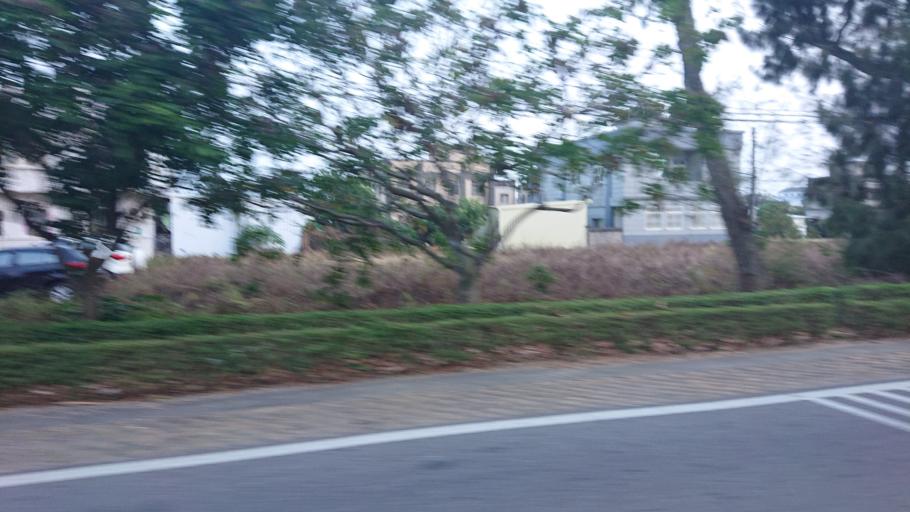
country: TW
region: Fukien
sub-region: Kinmen
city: Jincheng
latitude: 24.4602
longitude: 118.3242
